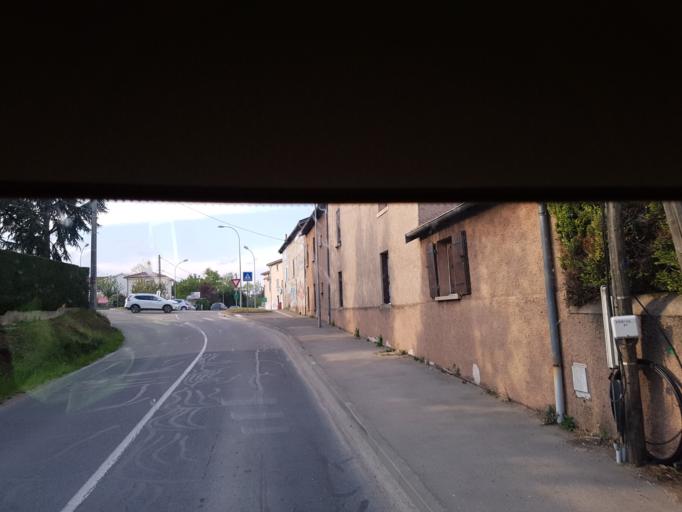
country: FR
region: Rhone-Alpes
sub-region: Departement du Rhone
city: Grezieu-la-Varenne
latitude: 45.7397
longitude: 4.6914
